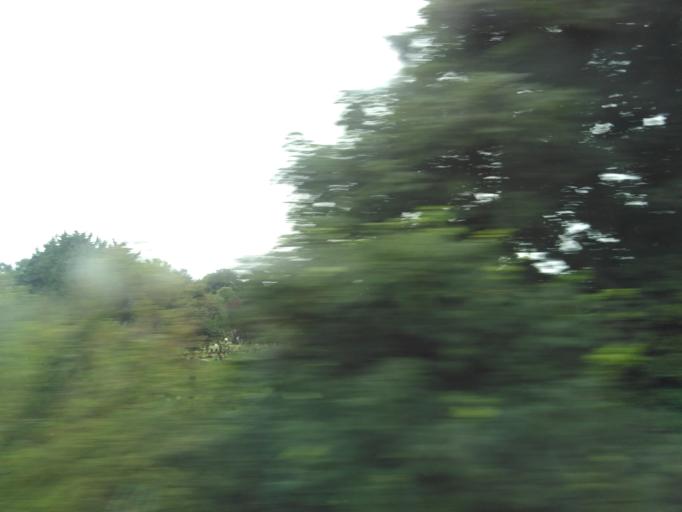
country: GB
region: Scotland
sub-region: East Lothian
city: Musselburgh
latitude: 55.9439
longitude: -3.0902
